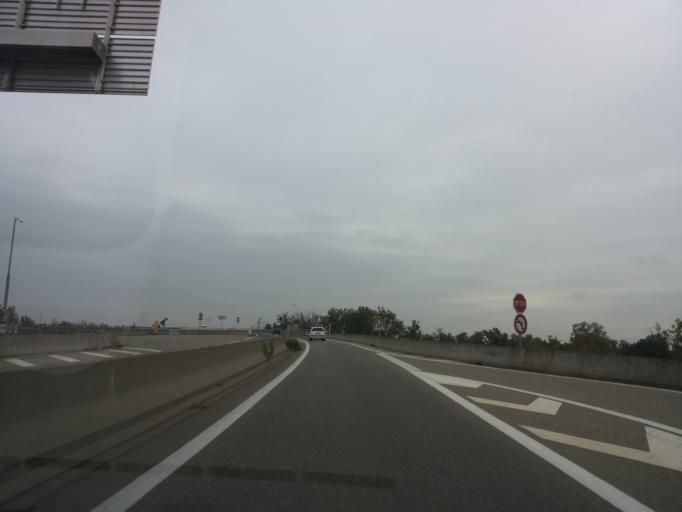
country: FR
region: Alsace
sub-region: Departement du Bas-Rhin
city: Plobsheim
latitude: 48.4933
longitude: 7.7615
